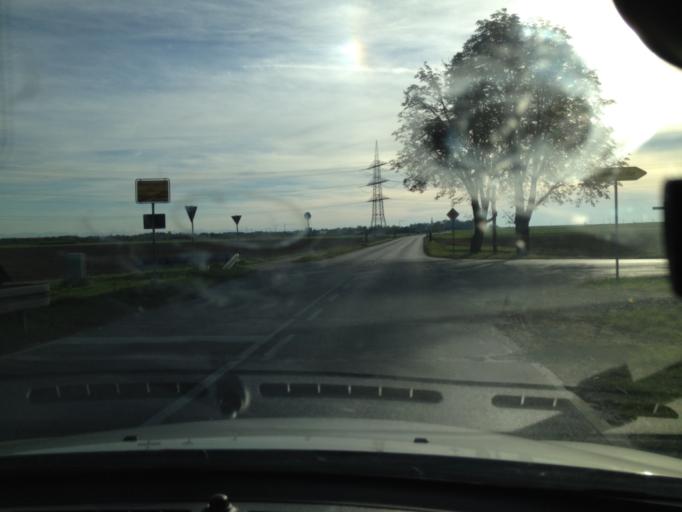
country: DE
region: Bavaria
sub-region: Swabia
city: Oberottmarshausen
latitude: 48.2337
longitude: 10.8536
